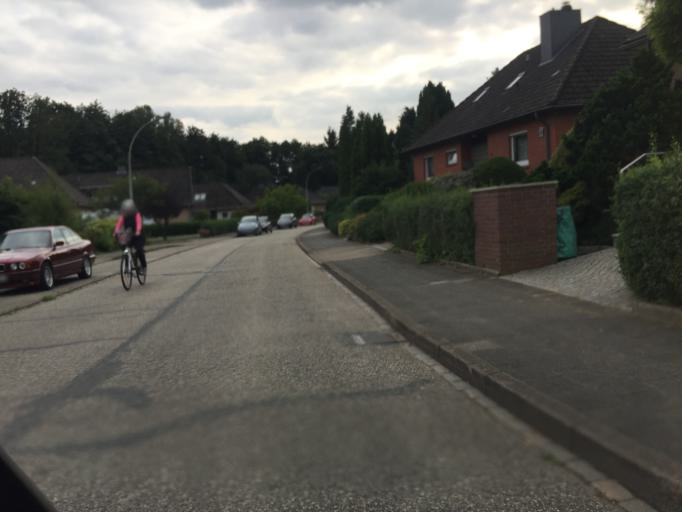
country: DE
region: Schleswig-Holstein
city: Itzehoe
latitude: 53.9455
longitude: 9.5093
